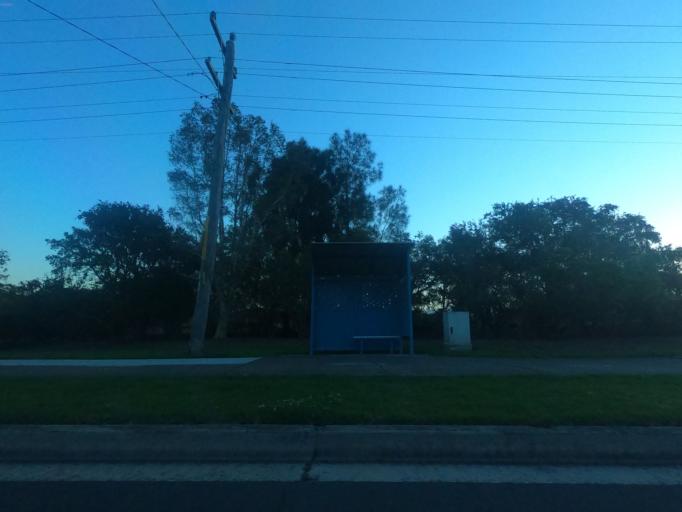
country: AU
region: New South Wales
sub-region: Wollongong
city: Koonawarra
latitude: -34.4941
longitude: 150.8180
